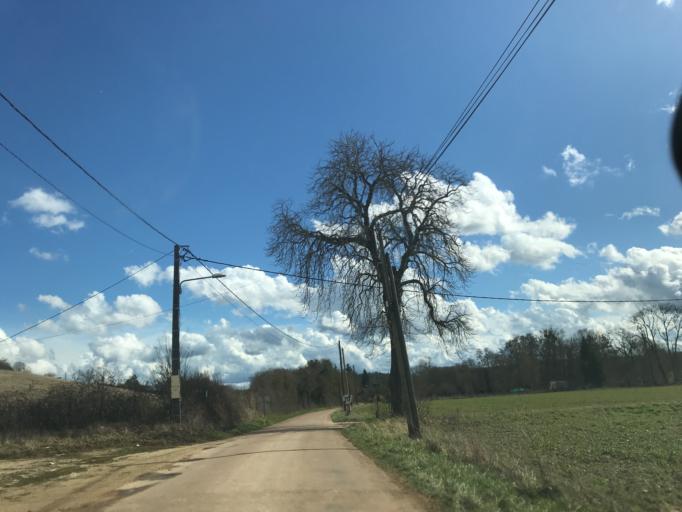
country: FR
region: Bourgogne
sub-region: Departement de l'Yonne
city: Fontenailles
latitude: 47.5113
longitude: 3.5047
